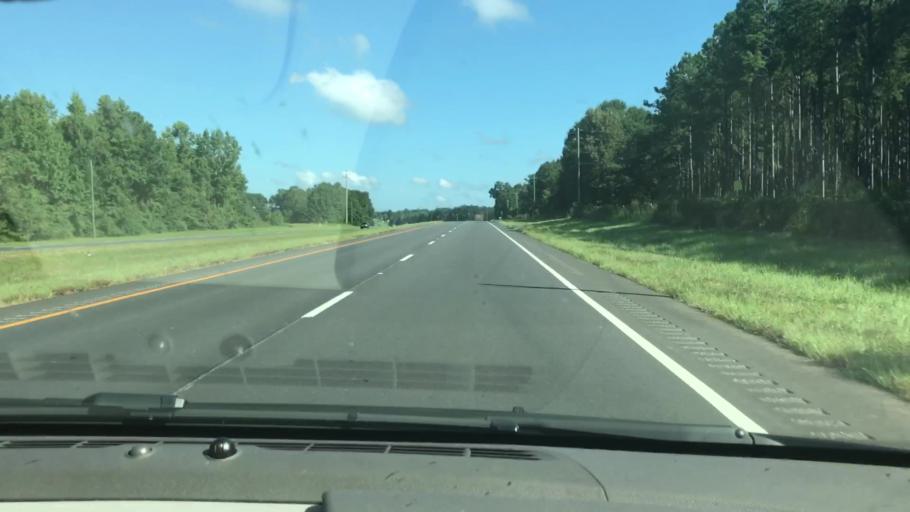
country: US
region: Alabama
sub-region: Barbour County
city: Eufaula
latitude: 32.0140
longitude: -85.1170
